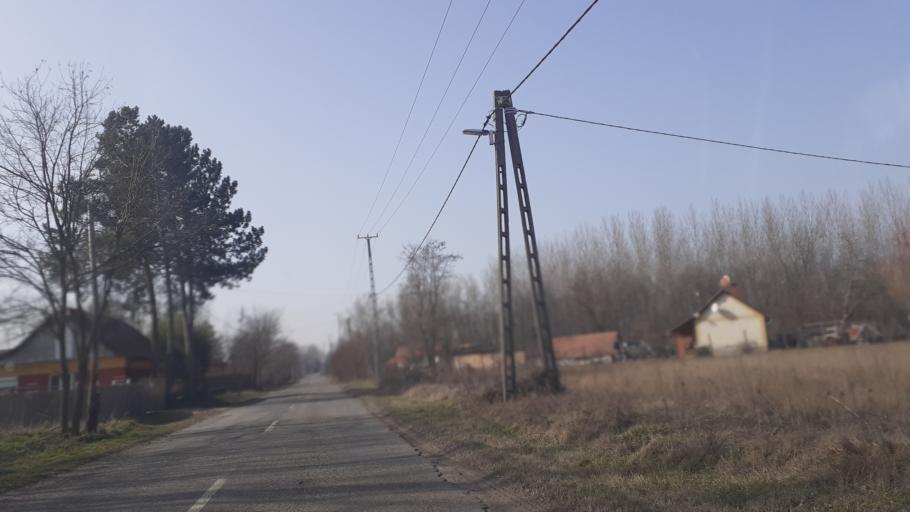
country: HU
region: Bacs-Kiskun
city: Kunszentmiklos
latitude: 47.0215
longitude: 19.2037
